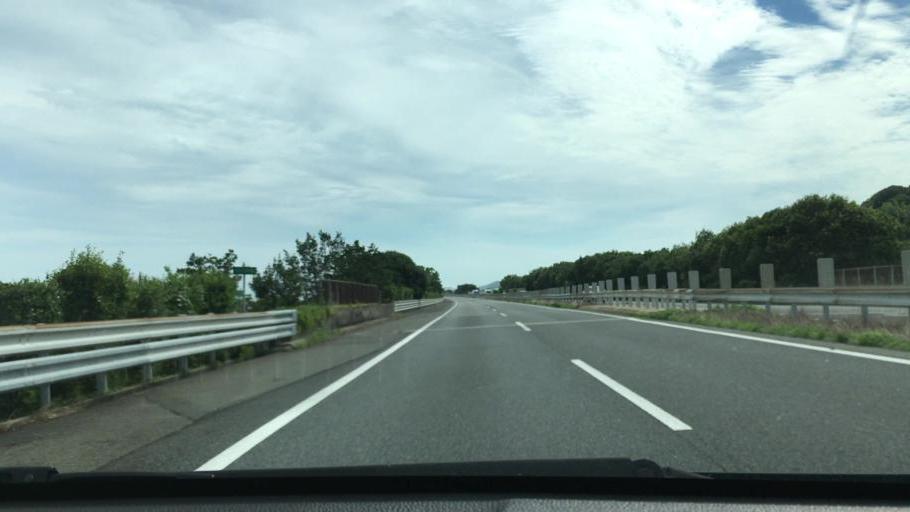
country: JP
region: Yamaguchi
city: Hofu
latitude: 34.0641
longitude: 131.5492
